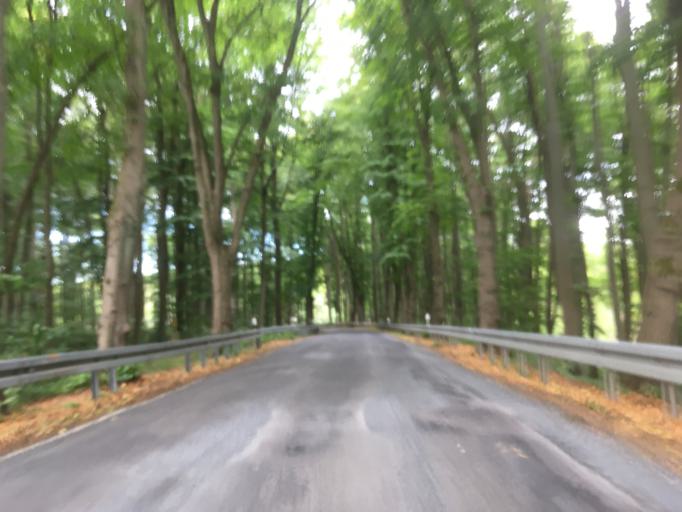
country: DE
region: Brandenburg
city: Mittenwalde
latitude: 53.2423
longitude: 13.5935
